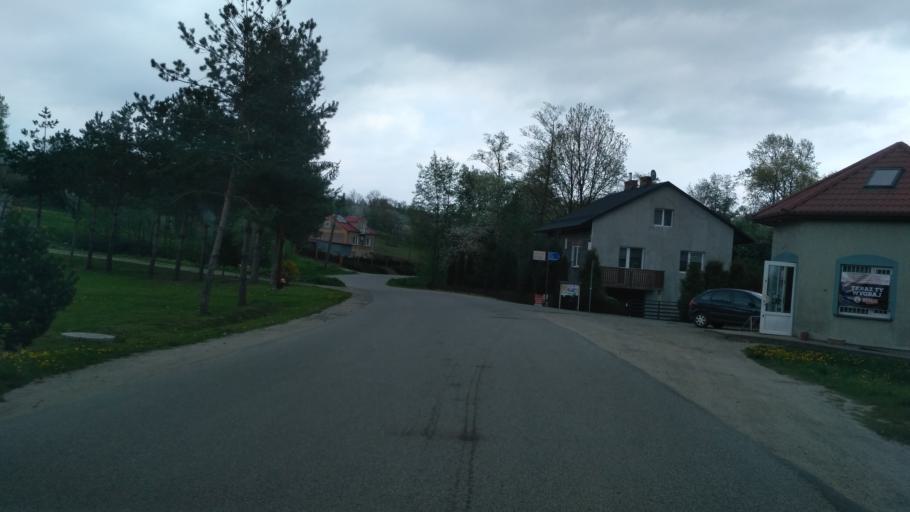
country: PL
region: Subcarpathian Voivodeship
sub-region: Powiat debicki
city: Leki Gorne
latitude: 49.9737
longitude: 21.1794
